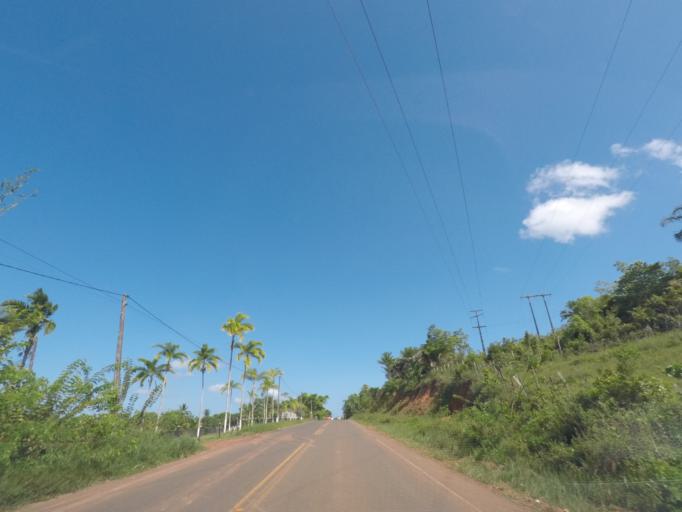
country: BR
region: Bahia
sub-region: Camamu
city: Camamu
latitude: -13.9265
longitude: -39.1191
